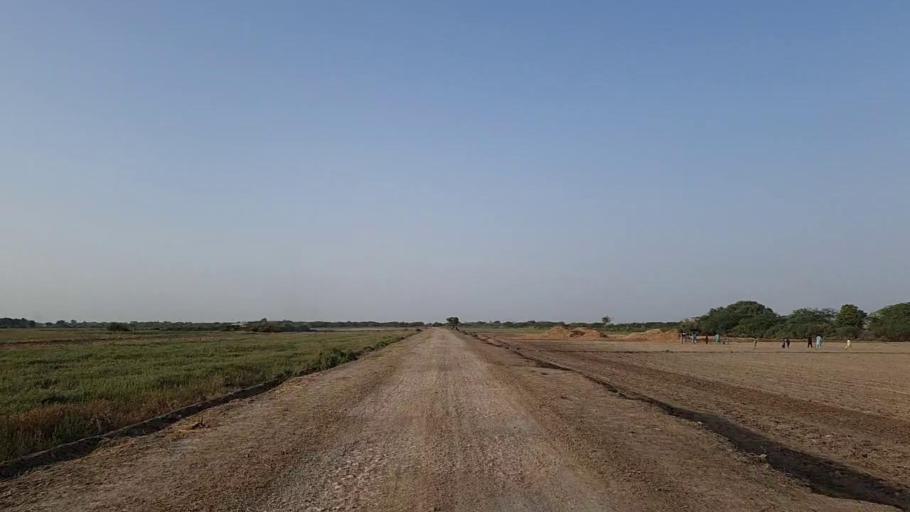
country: PK
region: Sindh
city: Jati
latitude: 24.3782
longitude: 68.1480
